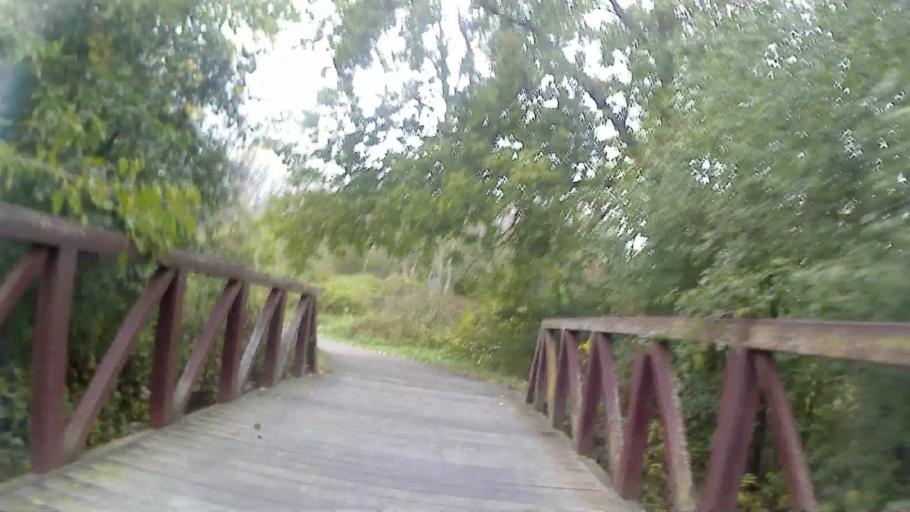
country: US
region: Illinois
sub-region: Kane County
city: Sugar Grove
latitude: 41.7752
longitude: -88.4148
